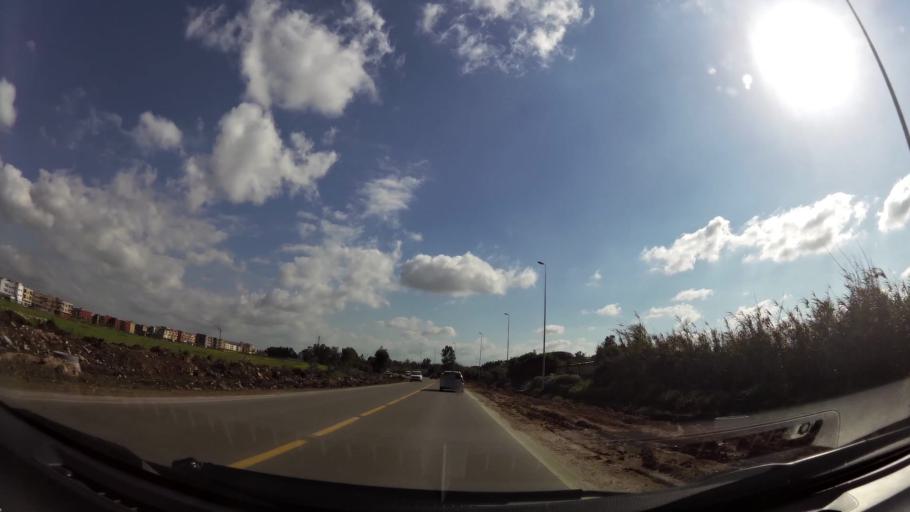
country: MA
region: Grand Casablanca
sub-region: Mediouna
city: Mediouna
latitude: 33.3808
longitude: -7.5398
